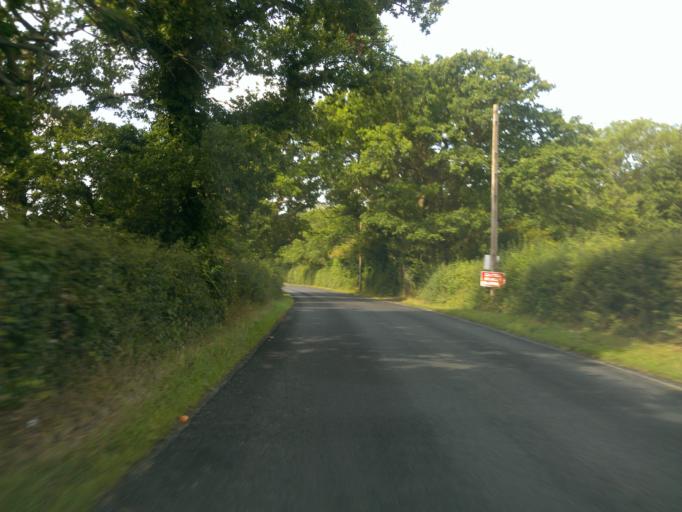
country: GB
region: England
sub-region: Kent
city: Edenbridge
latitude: 51.2019
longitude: 0.1459
